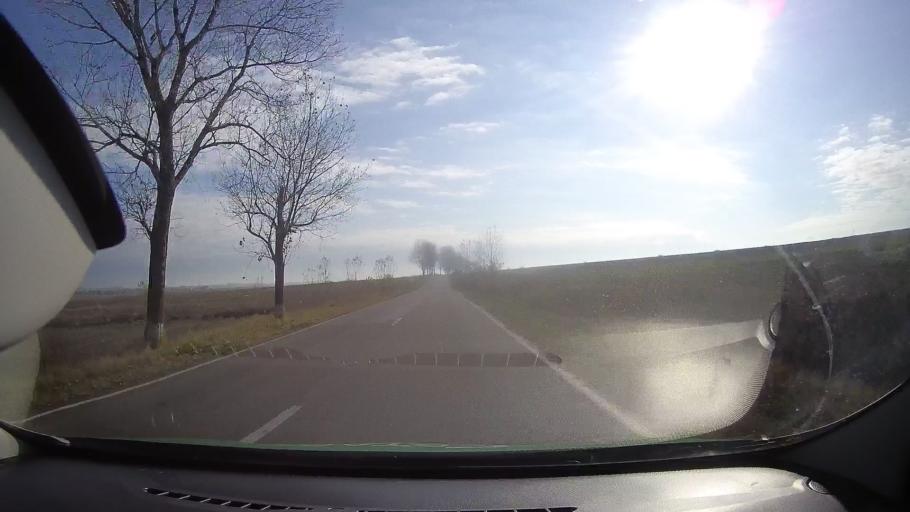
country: RO
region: Tulcea
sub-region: Comuna Mahmudia
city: Mahmudia
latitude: 45.0679
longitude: 29.1030
